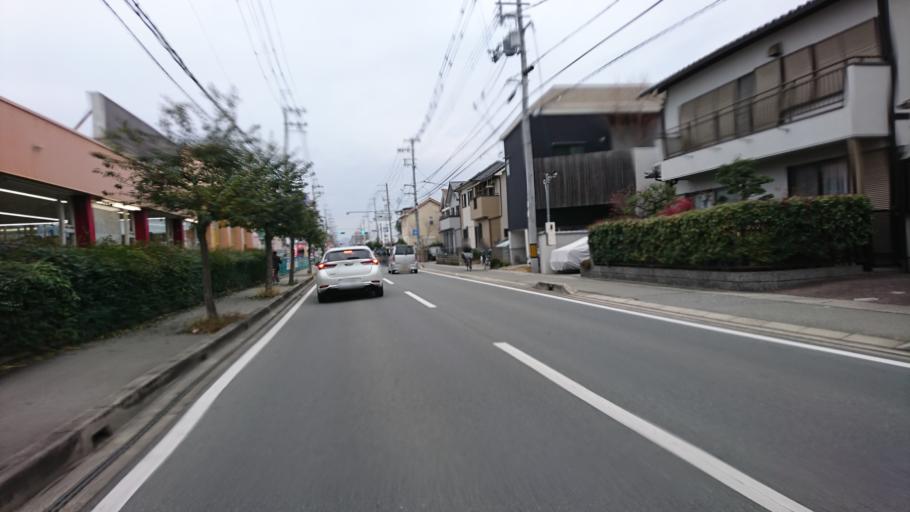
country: JP
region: Hyogo
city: Kakogawacho-honmachi
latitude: 34.7629
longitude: 134.8309
